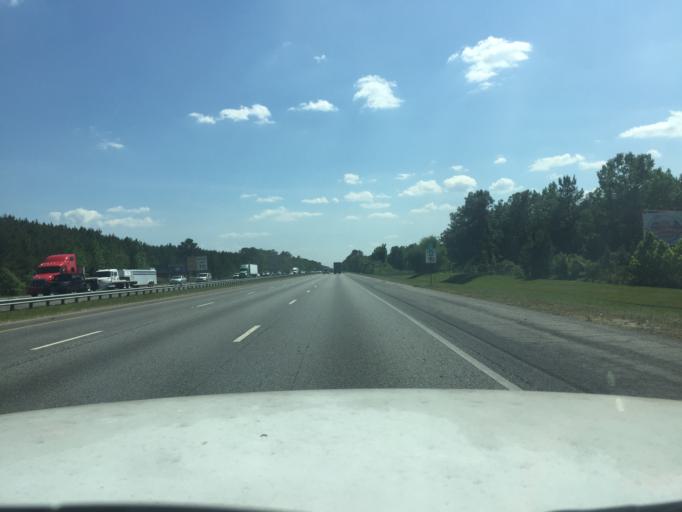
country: US
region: Georgia
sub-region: Chatham County
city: Pooler
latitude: 32.0597
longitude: -81.2535
